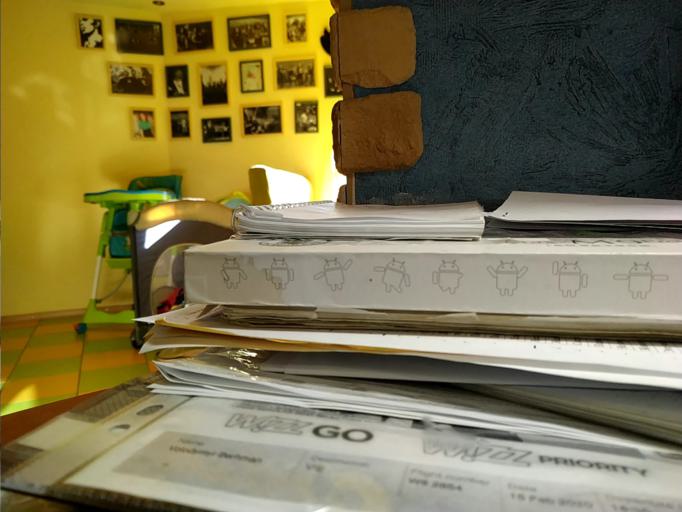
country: RU
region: Novgorod
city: Volot
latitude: 57.6112
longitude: 30.7911
